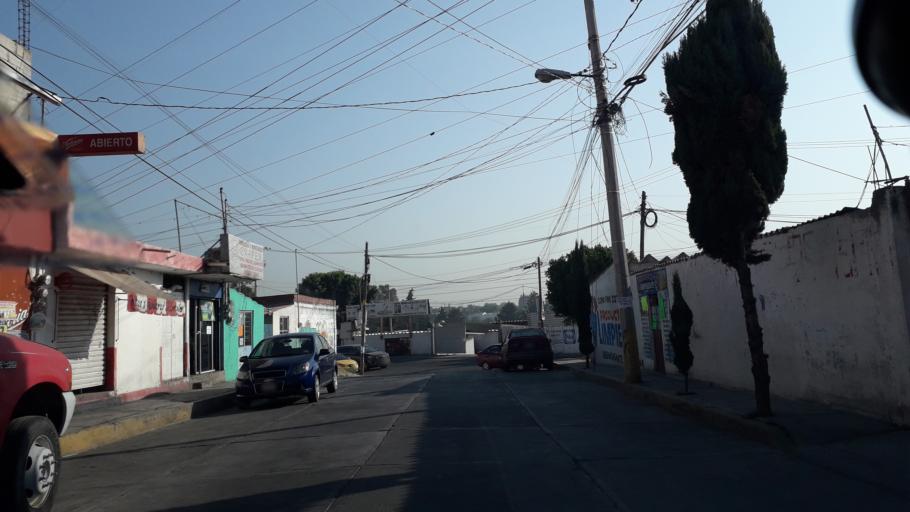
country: MX
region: Puebla
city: Tlazcalancingo
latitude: 19.0377
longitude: -98.2578
